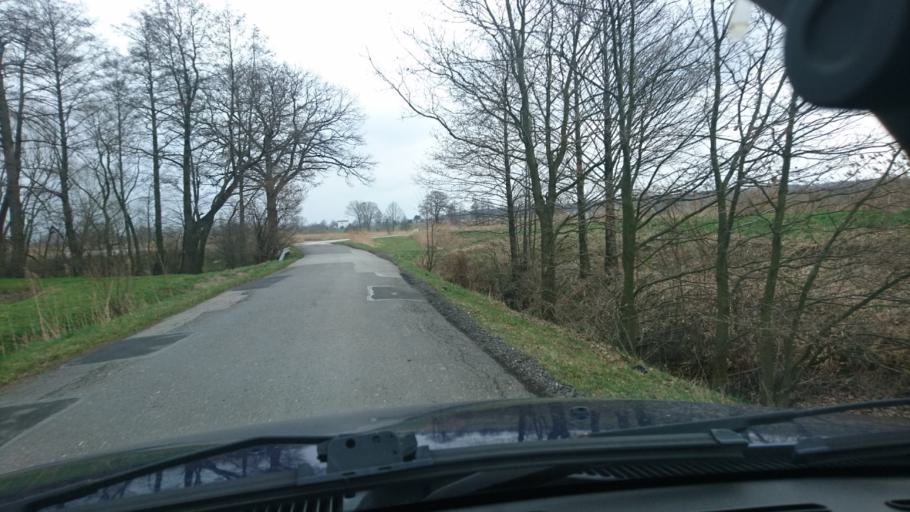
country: PL
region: Silesian Voivodeship
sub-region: Powiat bielski
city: Bronow
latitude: 49.8771
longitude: 18.8895
